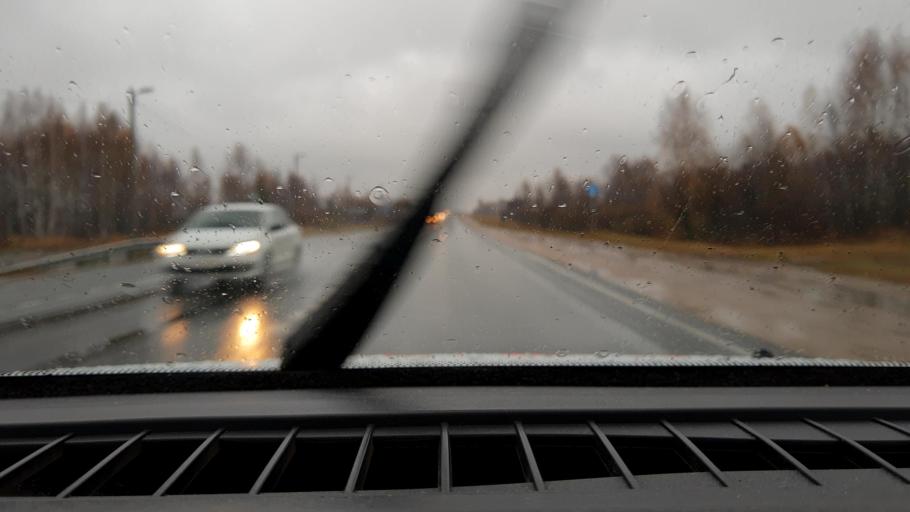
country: RU
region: Nizjnij Novgorod
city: Sitniki
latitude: 56.4877
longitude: 44.0210
